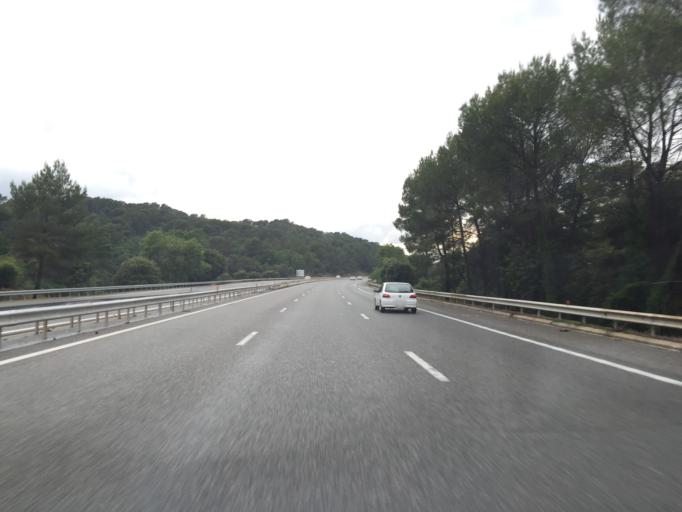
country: FR
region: Provence-Alpes-Cote d'Azur
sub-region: Departement du Var
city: Cabasse
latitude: 43.4066
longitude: 6.1891
